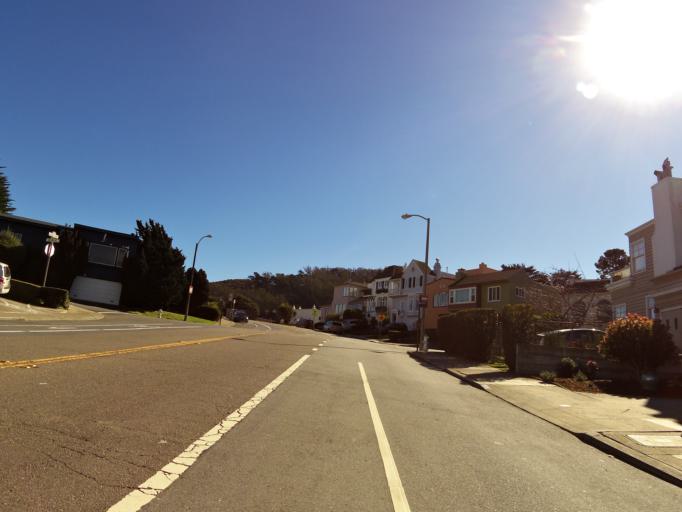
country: US
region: California
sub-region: San Mateo County
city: Daly City
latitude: 37.7444
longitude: -122.4567
